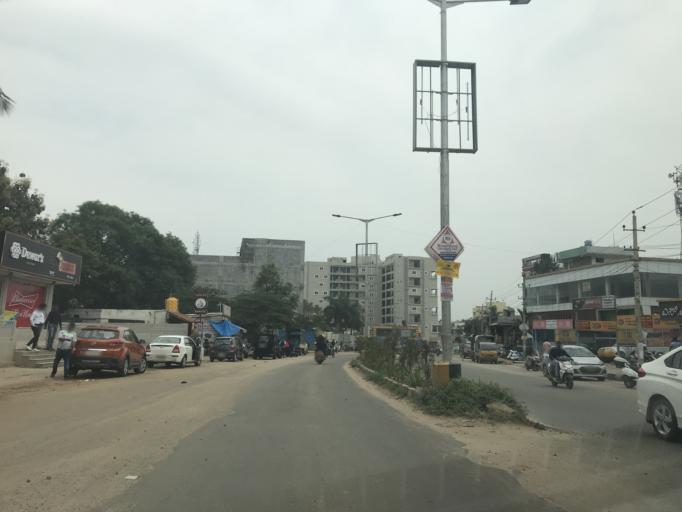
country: IN
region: Karnataka
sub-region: Bangalore Urban
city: Yelahanka
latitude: 13.0582
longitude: 77.6487
